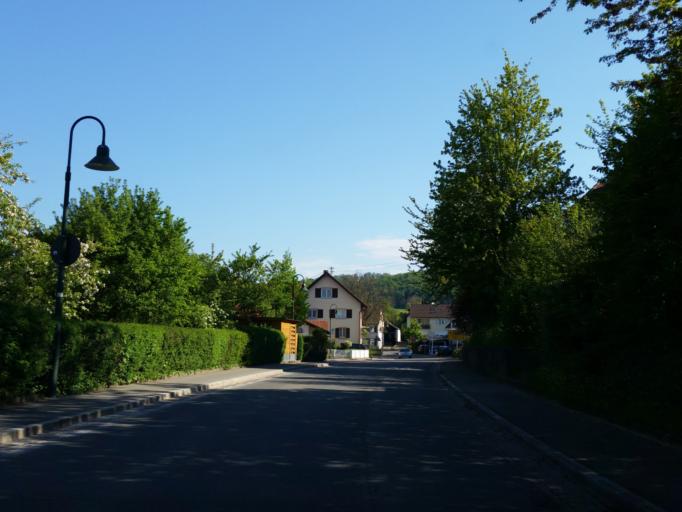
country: DE
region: Baden-Wuerttemberg
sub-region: Freiburg Region
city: Allensbach
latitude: 47.7338
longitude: 9.0747
